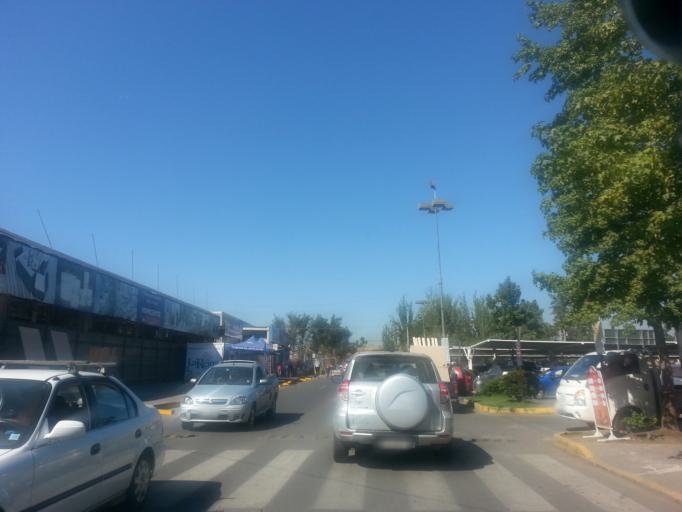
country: CL
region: Santiago Metropolitan
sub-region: Provincia de Santiago
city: Villa Presidente Frei, Nunoa, Santiago, Chile
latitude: -33.4624
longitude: -70.5456
